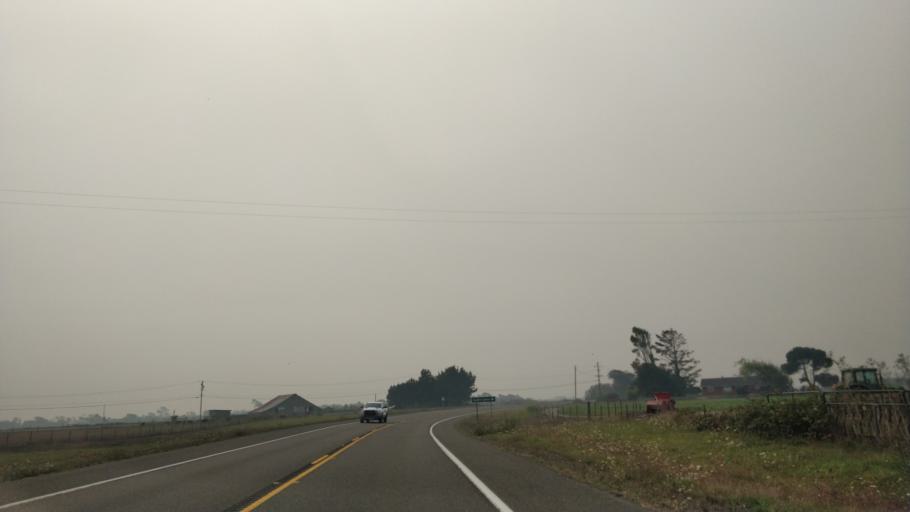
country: US
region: California
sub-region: Humboldt County
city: Fortuna
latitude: 40.6013
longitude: -124.2122
